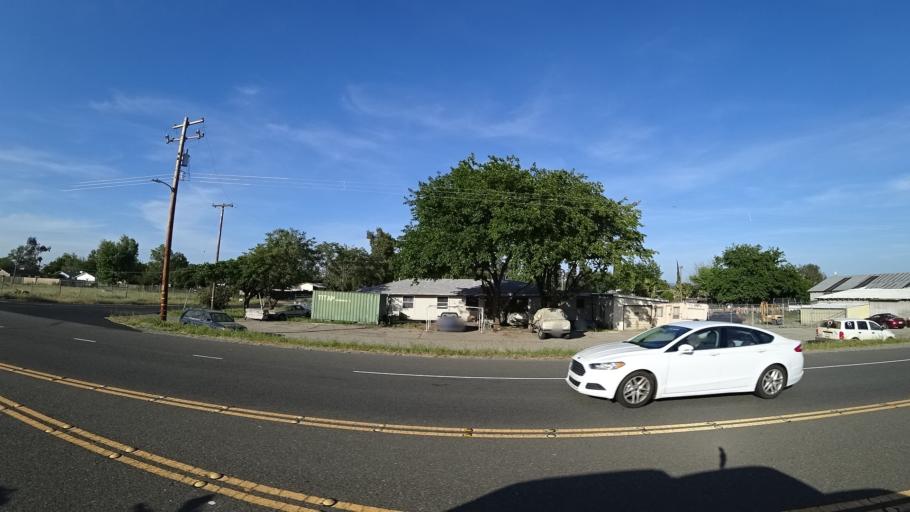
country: US
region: California
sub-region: Placer County
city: Sheridan
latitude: 38.9785
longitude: -121.3748
